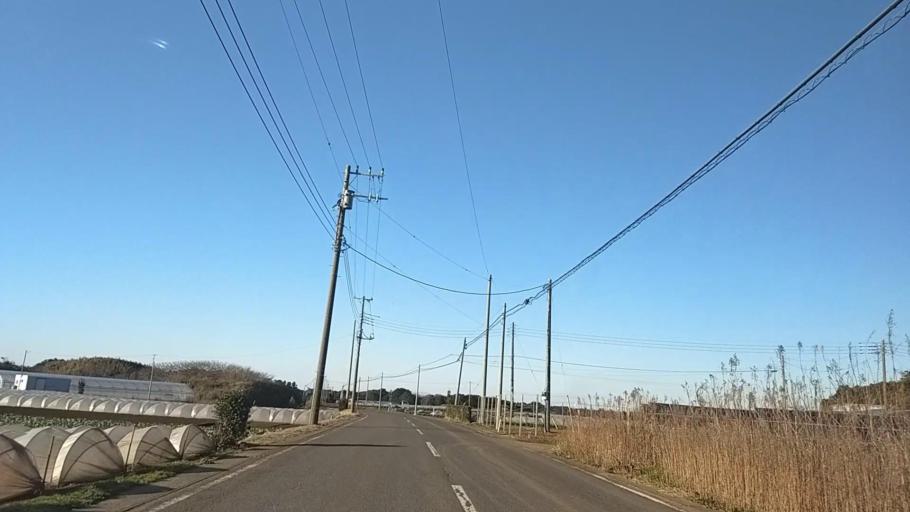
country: JP
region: Chiba
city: Asahi
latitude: 35.7385
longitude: 140.7375
